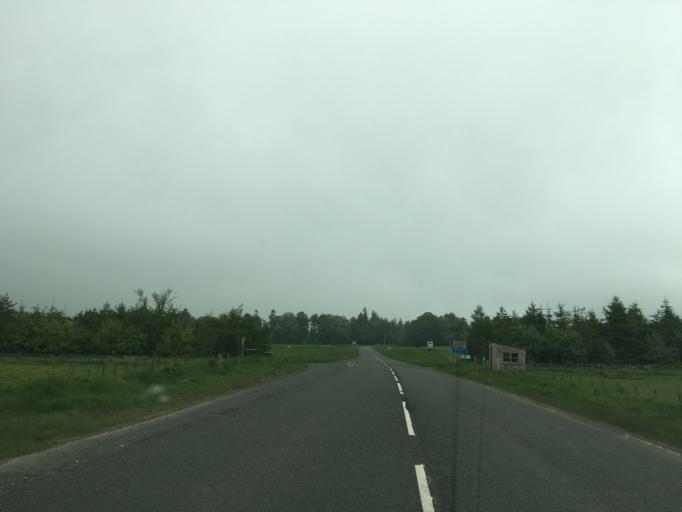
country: GB
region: Scotland
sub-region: The Scottish Borders
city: West Linton
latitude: 55.7279
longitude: -3.3198
